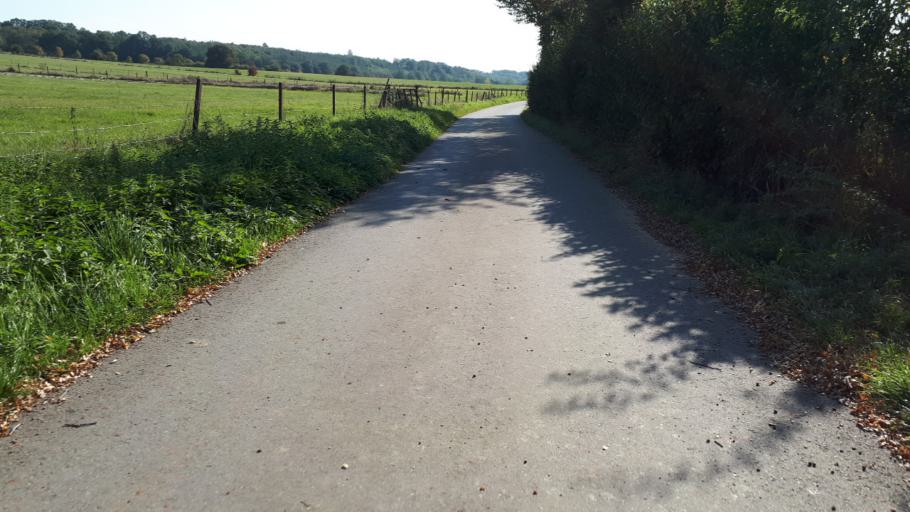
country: LU
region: Luxembourg
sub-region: Canton de Capellen
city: Kehlen
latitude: 49.6607
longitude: 6.0307
